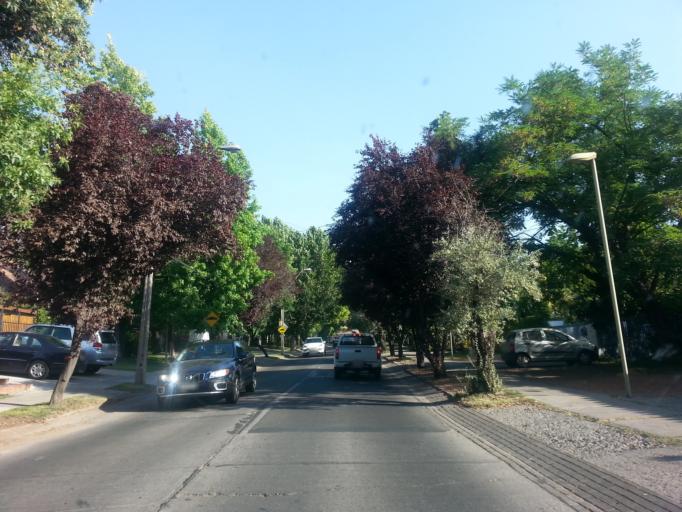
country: CL
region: Santiago Metropolitan
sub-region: Provincia de Santiago
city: Villa Presidente Frei, Nunoa, Santiago, Chile
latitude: -33.3766
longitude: -70.5082
